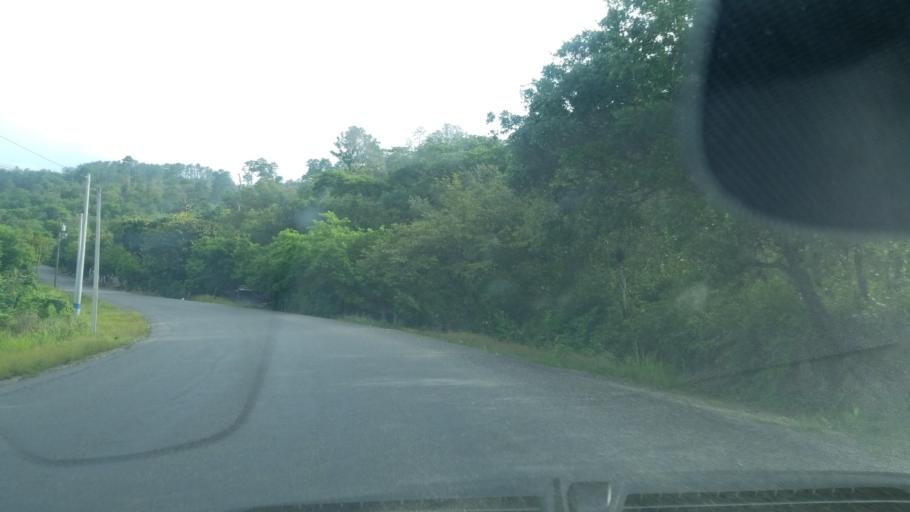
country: HN
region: Santa Barbara
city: Trinidad
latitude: 15.1677
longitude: -88.2599
